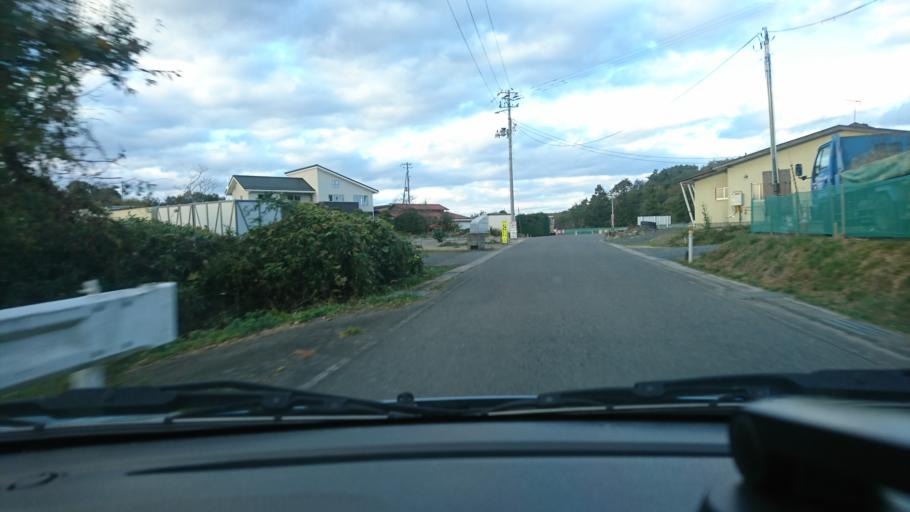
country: JP
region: Iwate
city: Ichinoseki
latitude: 38.7827
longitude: 141.2161
